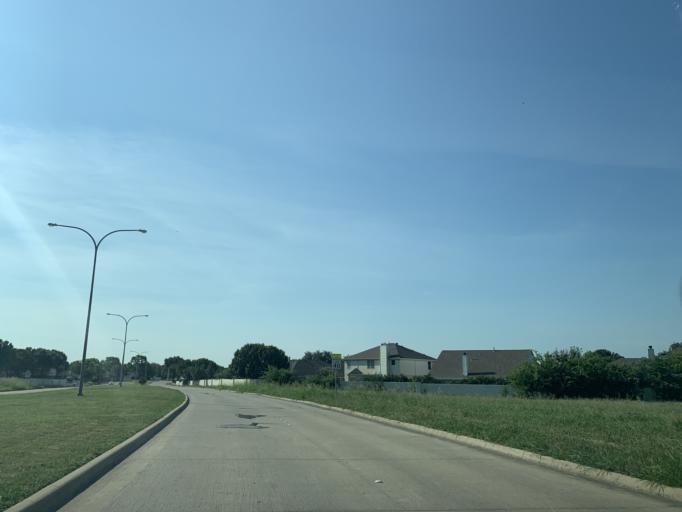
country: US
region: Texas
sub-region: Tarrant County
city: Blue Mound
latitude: 32.8798
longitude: -97.3065
